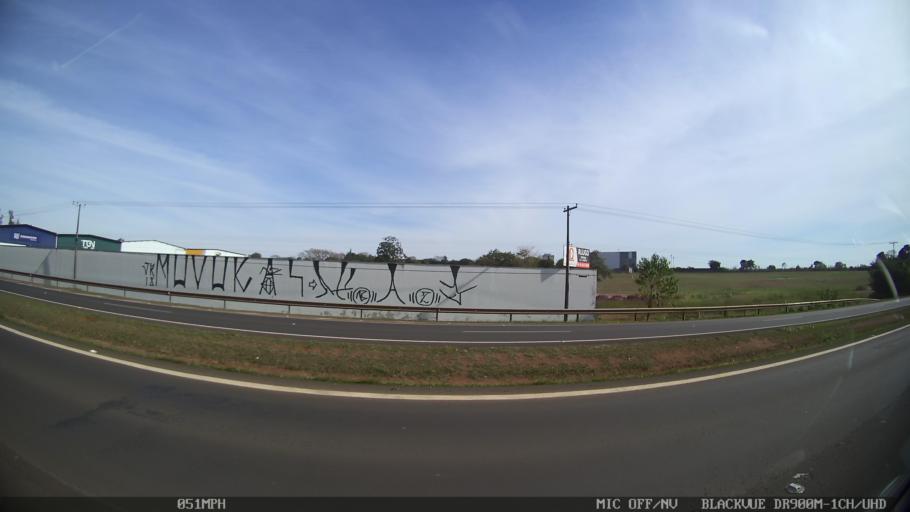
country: BR
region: Sao Paulo
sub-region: Piracicaba
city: Piracicaba
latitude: -22.7722
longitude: -47.6484
